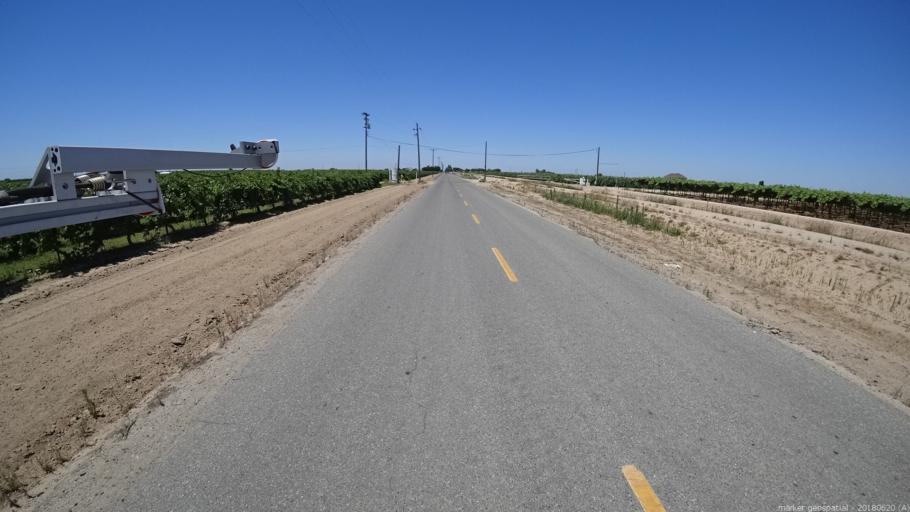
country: US
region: California
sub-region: Fresno County
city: Biola
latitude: 36.8658
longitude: -119.9962
